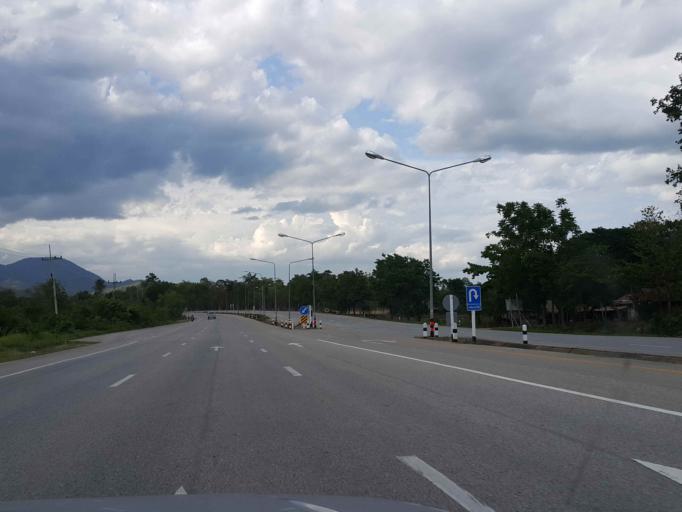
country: TH
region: Lampang
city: Thoen
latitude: 17.7354
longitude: 99.2331
